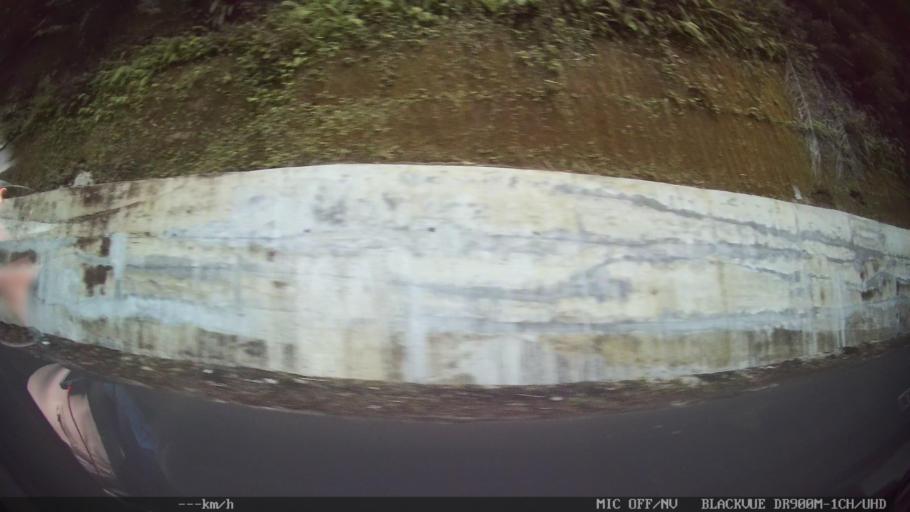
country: ID
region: Bali
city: Banjar Kubu
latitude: -8.4088
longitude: 115.4243
